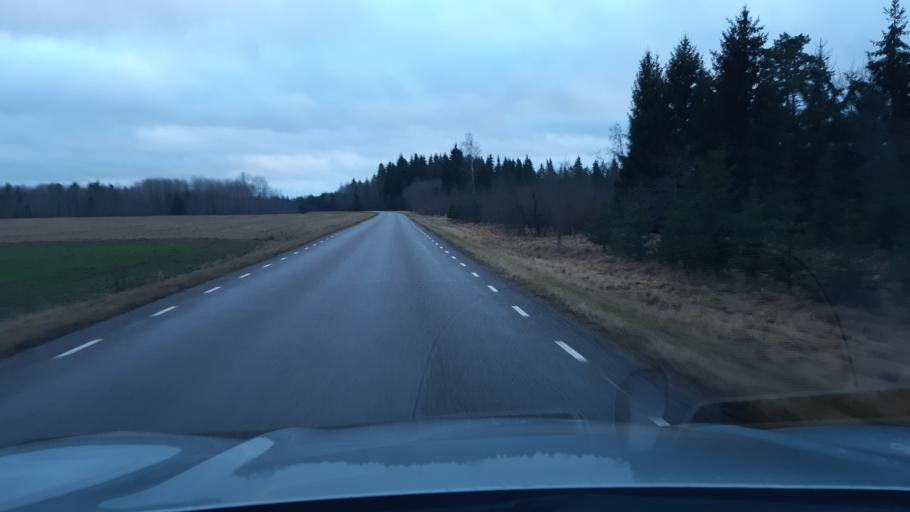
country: EE
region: Raplamaa
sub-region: Kohila vald
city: Kohila
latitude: 59.1462
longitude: 24.6535
